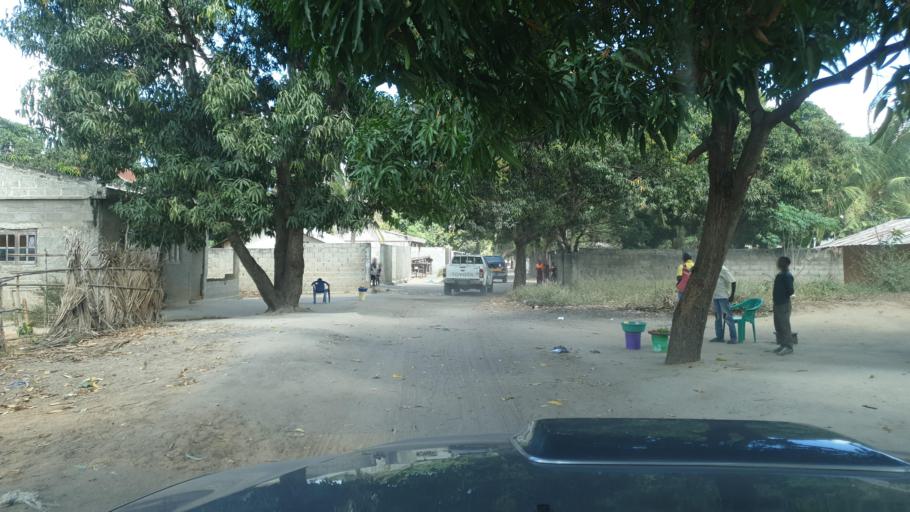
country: MZ
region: Nampula
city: Nacala
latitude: -14.5685
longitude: 40.7003
